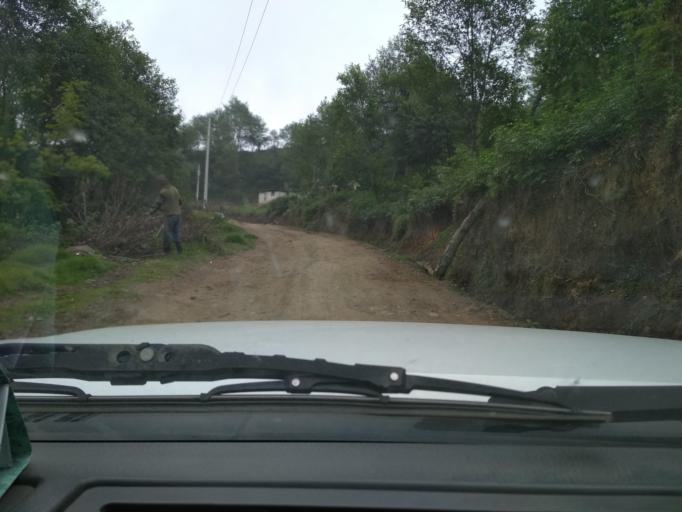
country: MX
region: Veracruz
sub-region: La Perla
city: Chilapa
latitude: 19.0010
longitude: -97.1690
